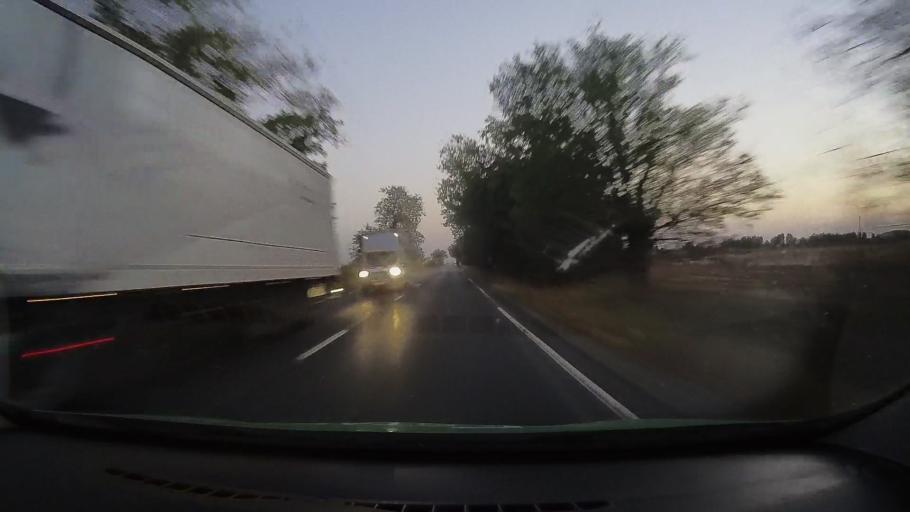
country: RO
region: Arad
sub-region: Comuna Livada
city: Livada
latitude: 46.2401
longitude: 21.3763
